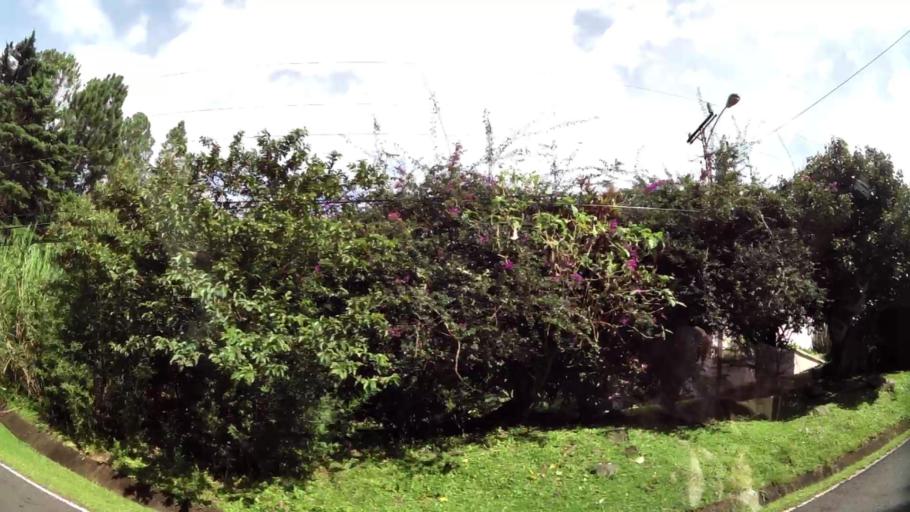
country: PA
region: Chiriqui
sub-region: Distrito Boquete
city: Boquete
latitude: 8.7886
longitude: -82.4261
